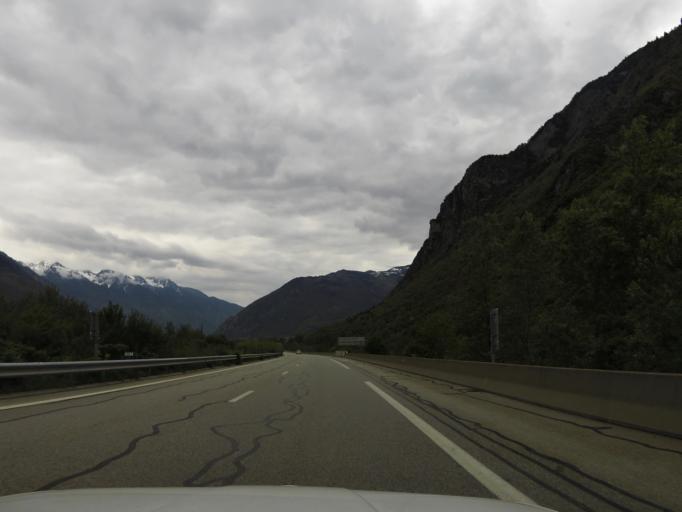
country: FR
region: Rhone-Alpes
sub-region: Departement de la Savoie
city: La Chambre
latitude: 45.3249
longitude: 6.3183
